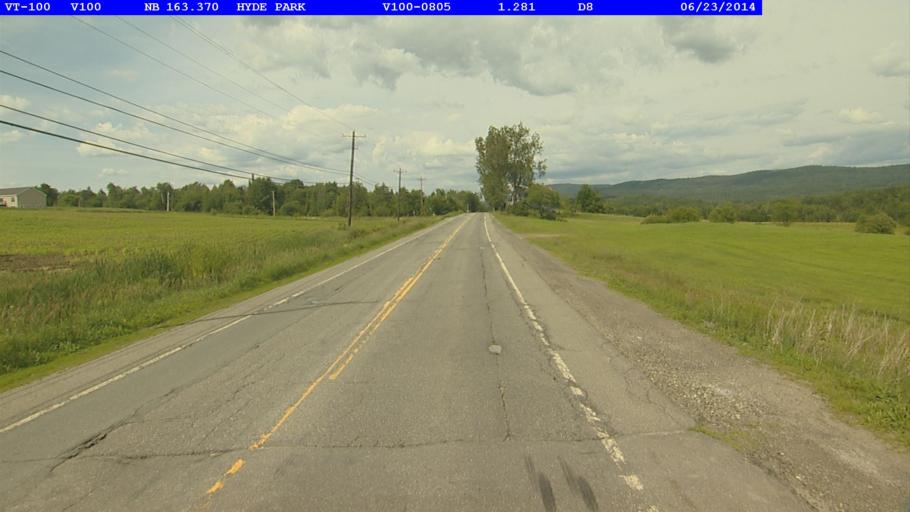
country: US
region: Vermont
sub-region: Lamoille County
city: Hyde Park
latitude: 44.6143
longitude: -72.6064
